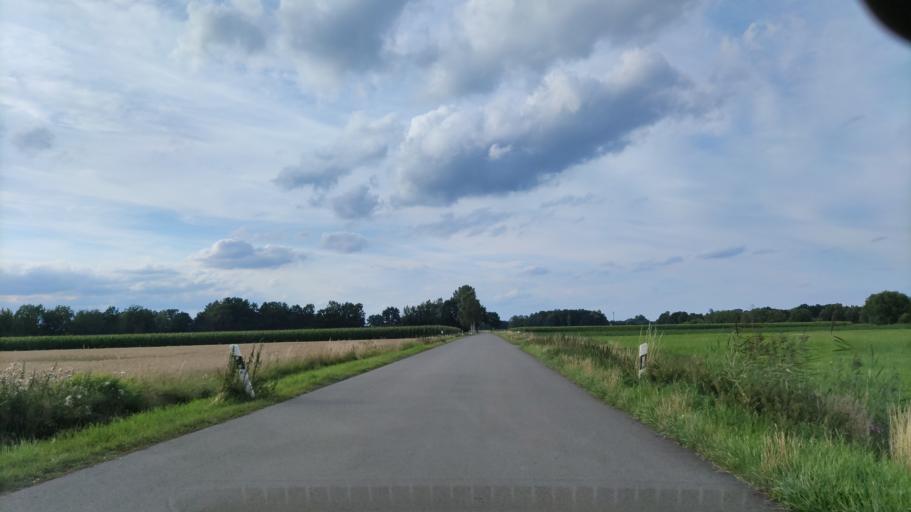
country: DE
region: Lower Saxony
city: Dannenberg
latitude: 53.0832
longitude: 11.1035
